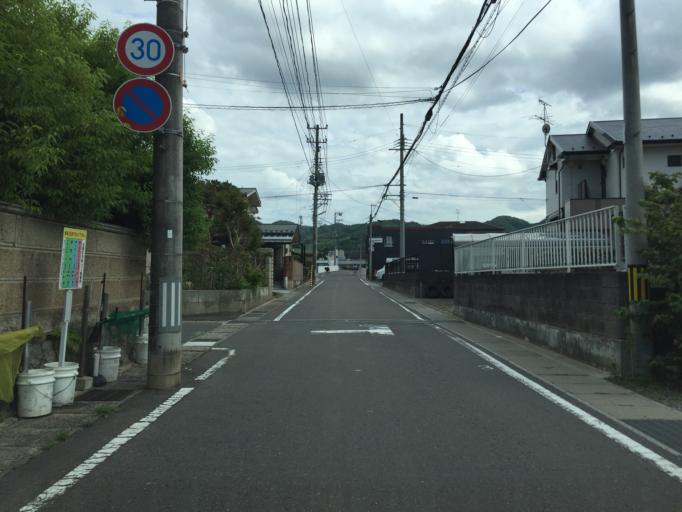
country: JP
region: Fukushima
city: Fukushima-shi
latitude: 37.7509
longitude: 140.4847
